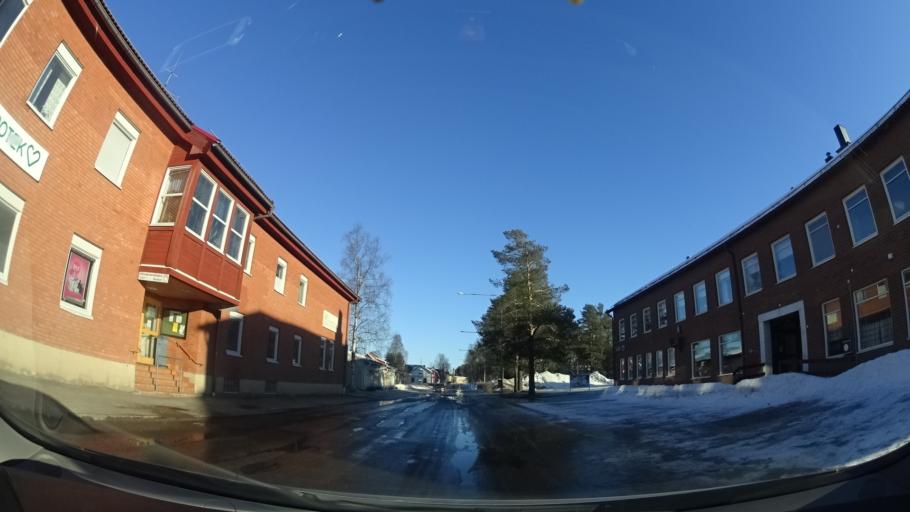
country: SE
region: Vaesterbotten
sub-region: Skelleftea Kommun
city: Langsele
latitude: 65.0592
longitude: 20.0390
